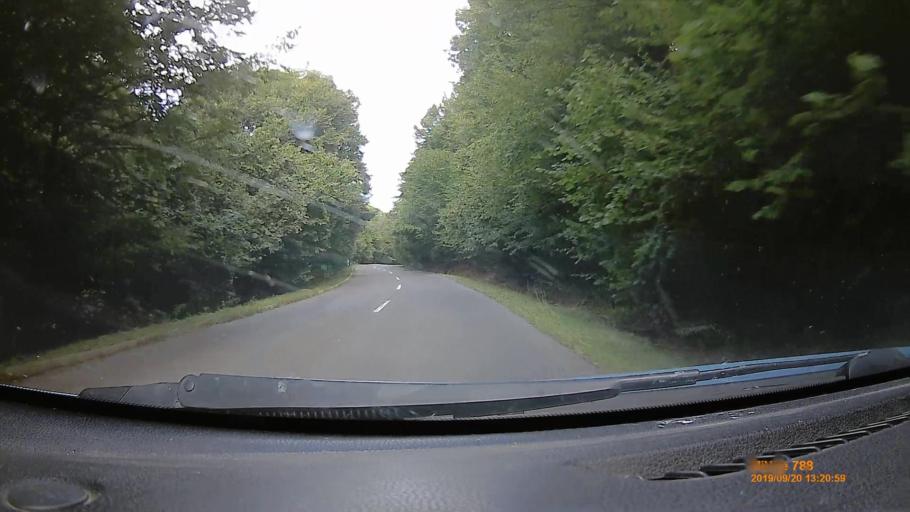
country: HU
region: Heves
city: Felsotarkany
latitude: 48.0178
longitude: 20.4689
